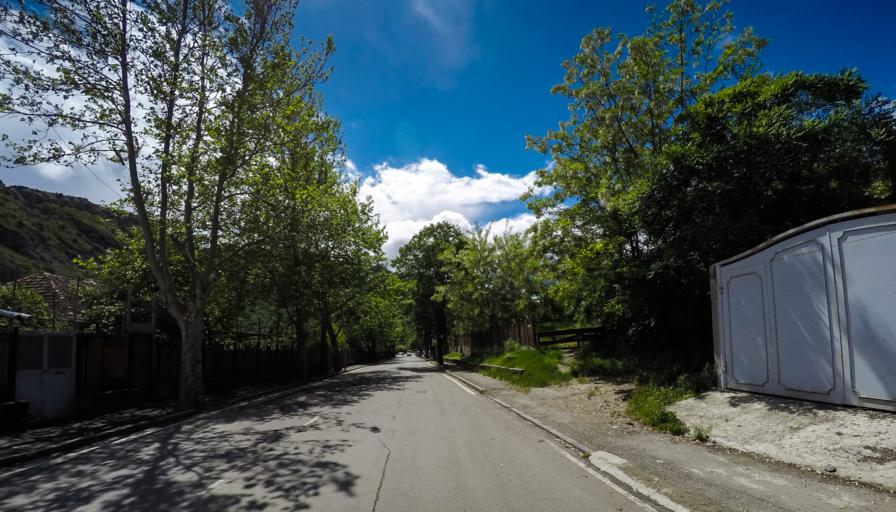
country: GE
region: Mtskheta-Mtianeti
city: Mtskheta
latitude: 41.8418
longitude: 44.7160
